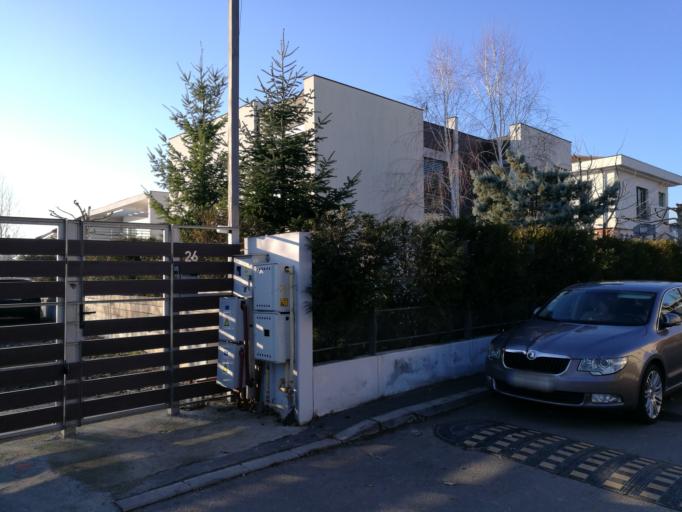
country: RO
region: Ilfov
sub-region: Comuna Otopeni
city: Otopeni
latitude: 44.5091
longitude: 26.0738
